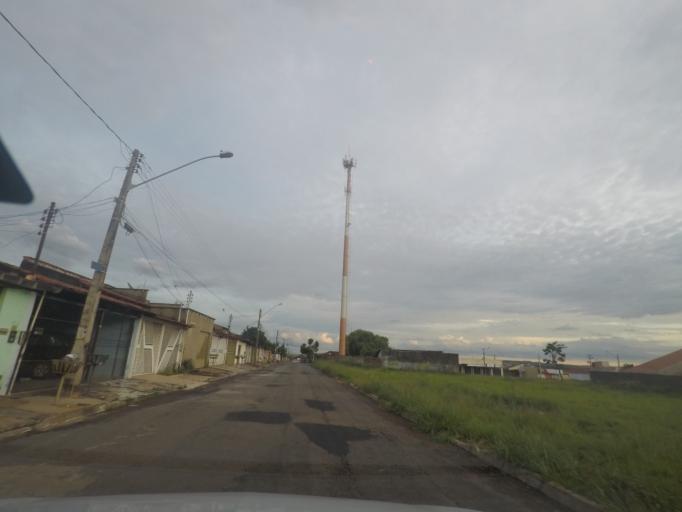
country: BR
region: Goias
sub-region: Goiania
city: Goiania
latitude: -16.7244
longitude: -49.3717
